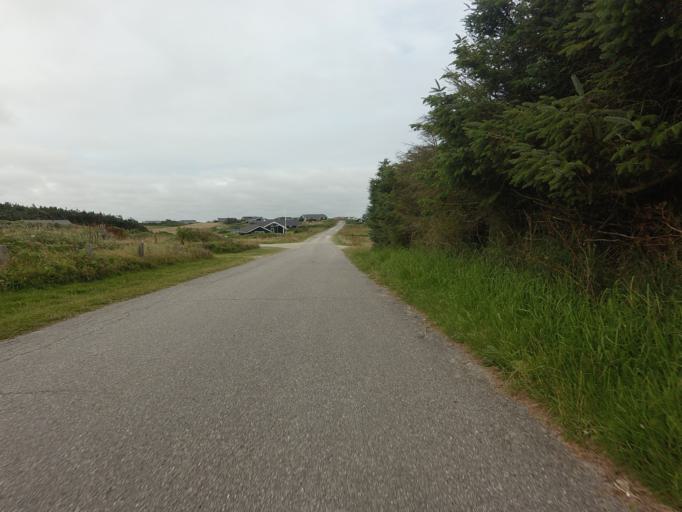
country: DK
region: North Denmark
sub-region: Jammerbugt Kommune
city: Pandrup
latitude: 57.3883
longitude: 9.7281
